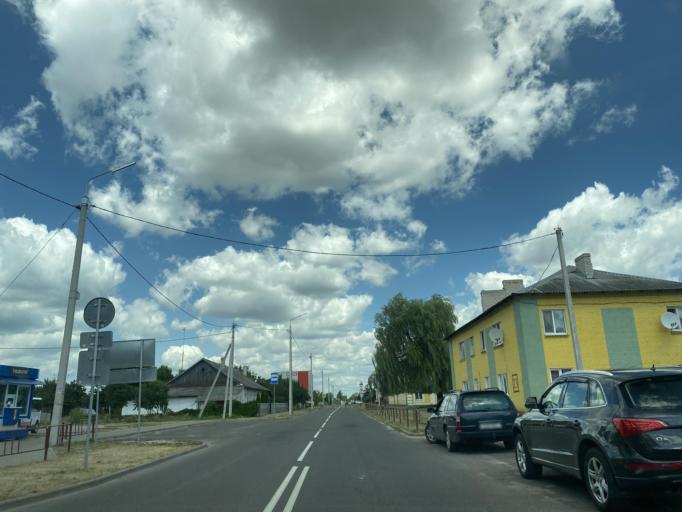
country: BY
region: Brest
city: Ivanava
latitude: 52.1496
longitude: 25.5421
